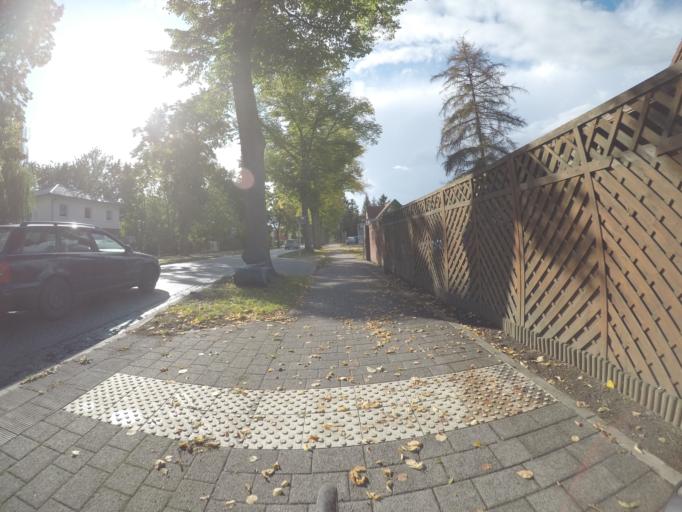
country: DE
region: Brandenburg
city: Petershagen
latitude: 52.5248
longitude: 13.7785
